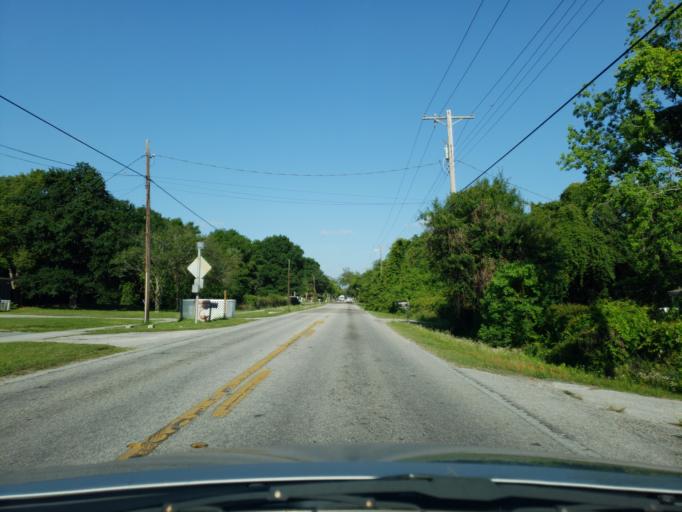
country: US
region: Florida
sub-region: Hillsborough County
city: Palm River-Clair Mel
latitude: 27.9431
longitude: -82.3879
